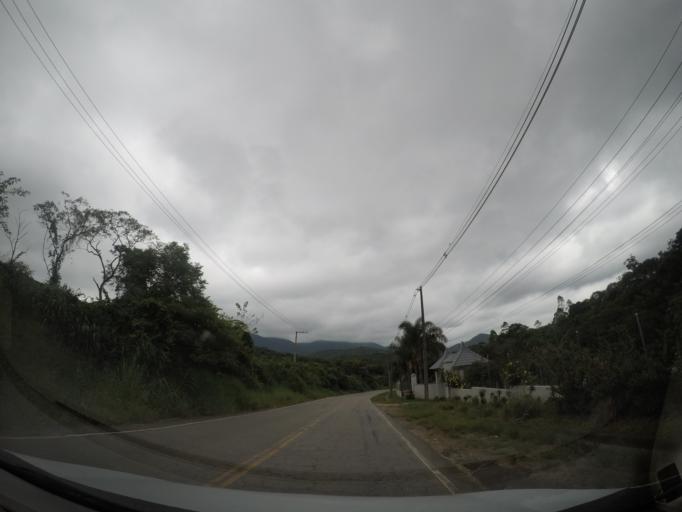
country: BR
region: Sao Paulo
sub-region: Aruja
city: Aruja
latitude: -23.3424
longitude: -46.4047
